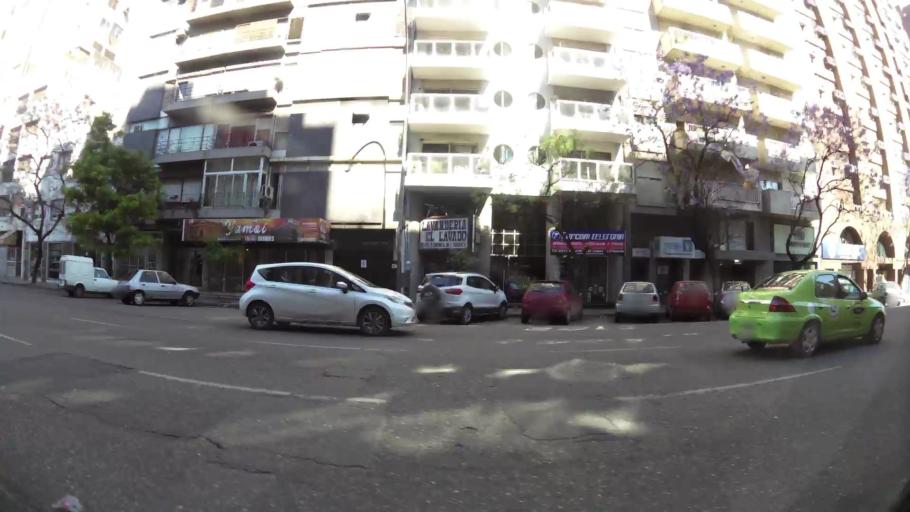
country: AR
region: Cordoba
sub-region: Departamento de Capital
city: Cordoba
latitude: -31.4175
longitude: -64.1803
